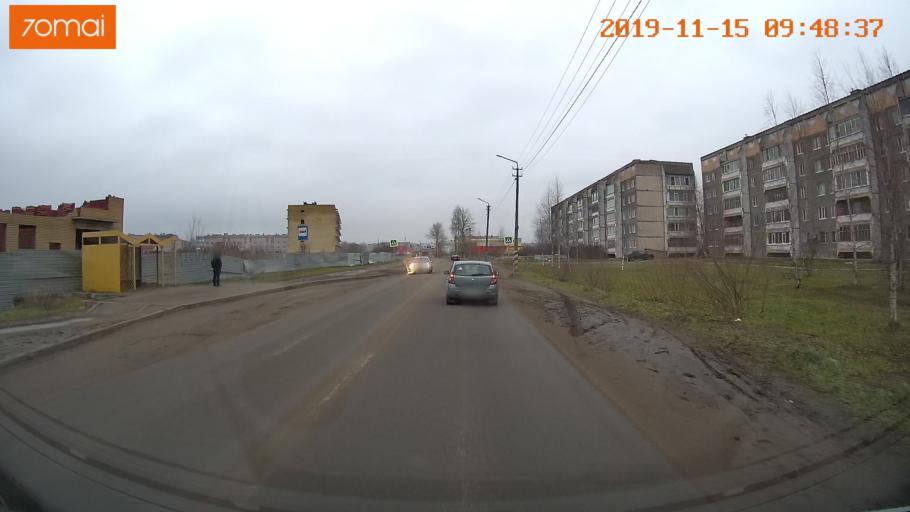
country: RU
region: Vologda
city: Sheksna
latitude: 59.2241
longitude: 38.5132
